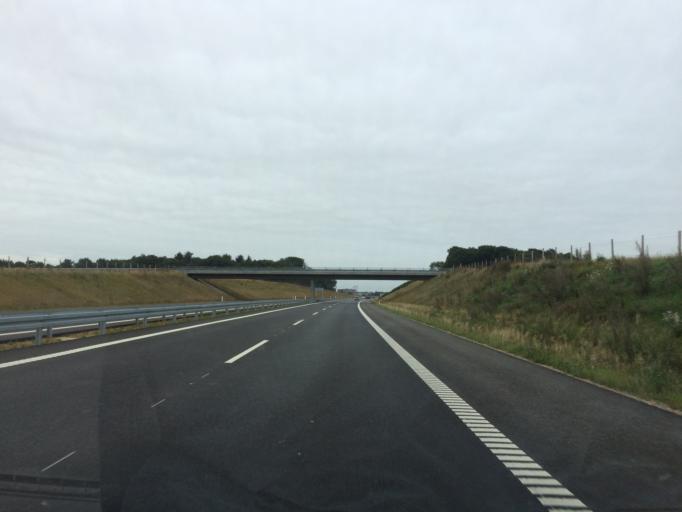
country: DK
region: Central Jutland
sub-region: Herning Kommune
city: Snejbjerg
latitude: 56.1761
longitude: 8.8922
